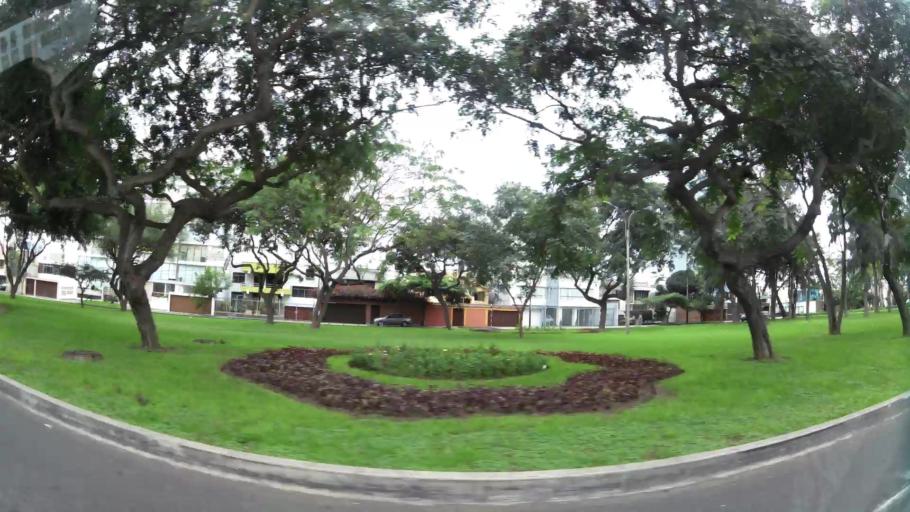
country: PE
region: Lima
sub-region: Lima
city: San Luis
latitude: -12.0926
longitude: -77.0170
